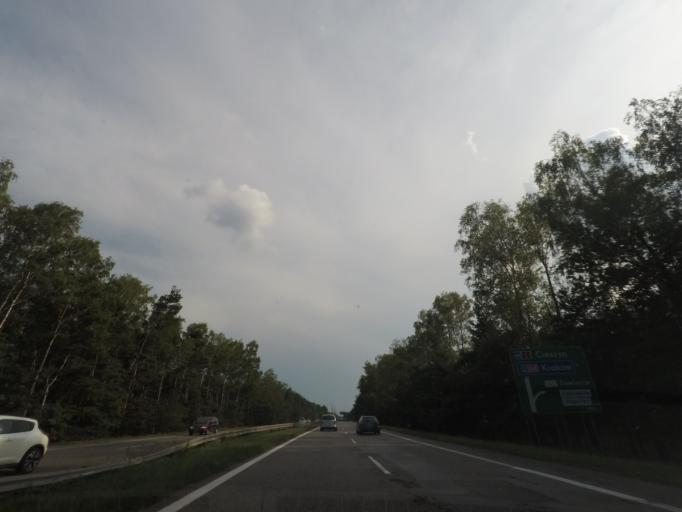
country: PL
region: Silesian Voivodeship
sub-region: Dabrowa Gornicza
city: Dabrowa Gornicza
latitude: 50.3659
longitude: 19.2506
